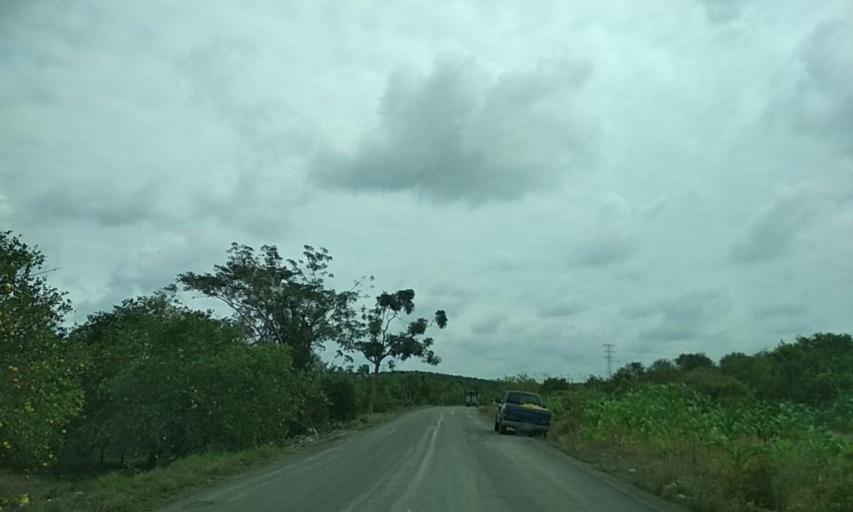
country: MX
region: Veracruz
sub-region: Papantla
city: El Chote
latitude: 20.3523
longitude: -97.3561
